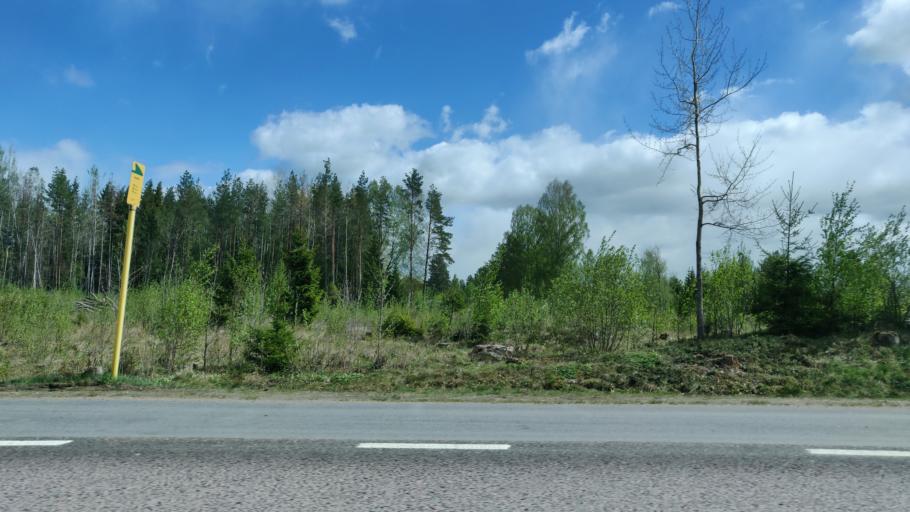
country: SE
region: Vaermland
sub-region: Karlstads Kommun
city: Skattkarr
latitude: 59.5224
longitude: 13.6174
